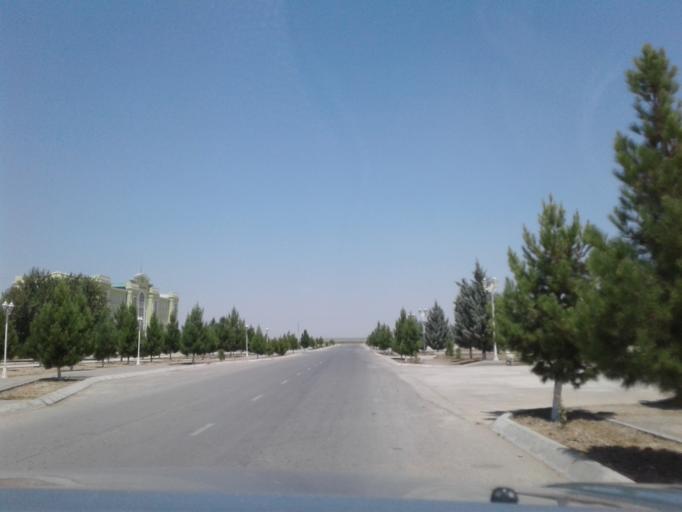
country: IR
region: Razavi Khorasan
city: Dargaz
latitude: 37.6498
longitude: 59.1489
